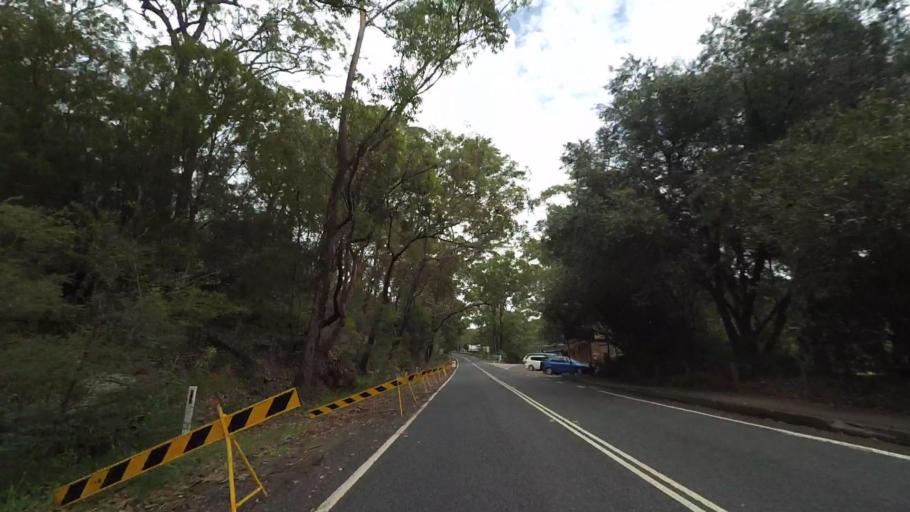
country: AU
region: New South Wales
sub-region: Sutherland Shire
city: Loftus
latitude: -34.0746
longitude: 151.0570
